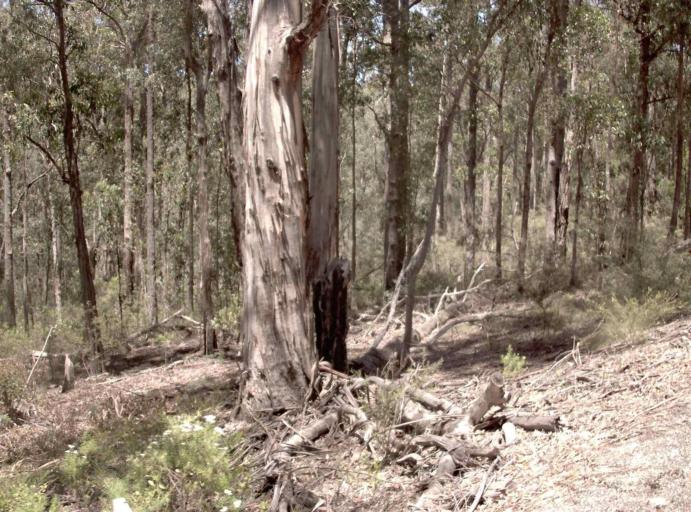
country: AU
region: Victoria
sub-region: East Gippsland
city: Lakes Entrance
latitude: -37.5964
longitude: 147.8906
